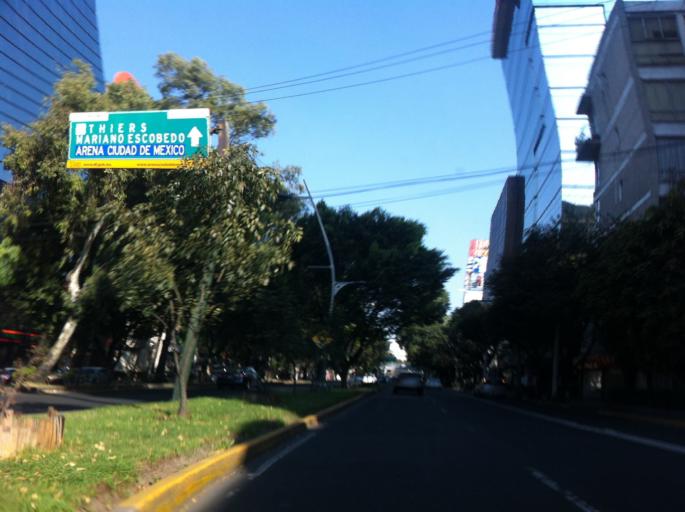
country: MX
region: Mexico City
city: Miguel Hidalgo
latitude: 19.4378
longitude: -99.1890
